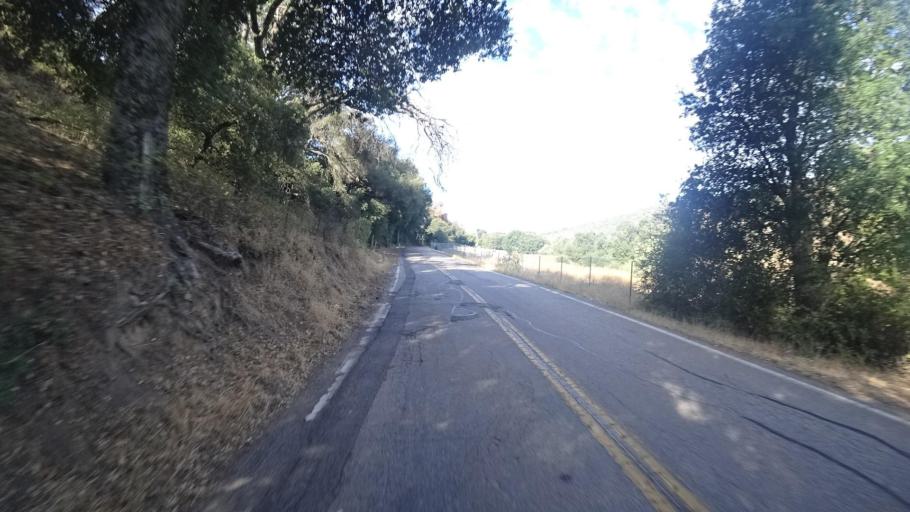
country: US
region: California
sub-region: San Diego County
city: Ramona
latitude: 33.1982
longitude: -116.7593
